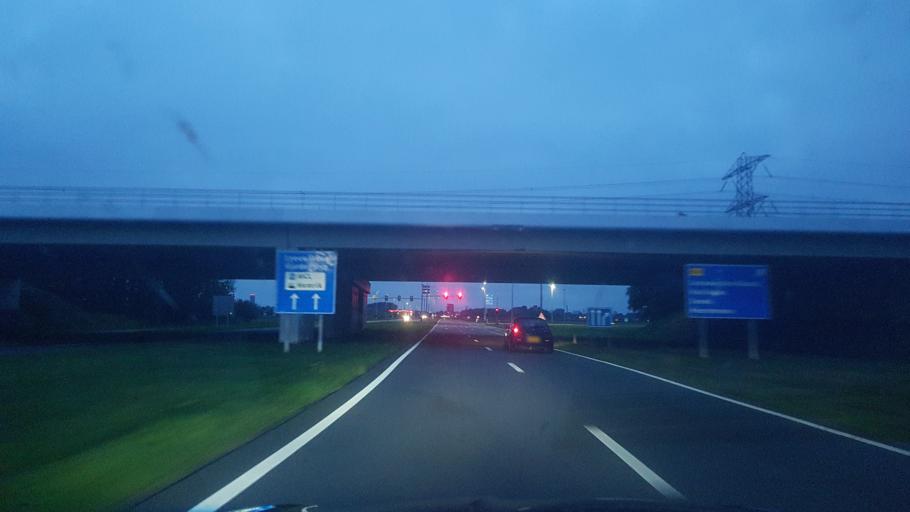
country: NL
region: Friesland
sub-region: Gemeente Boarnsterhim
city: Wergea
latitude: 53.1662
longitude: 5.8304
